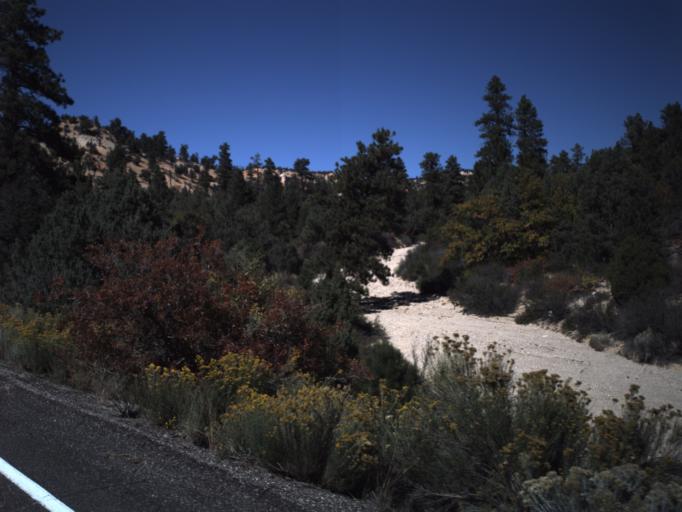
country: US
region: Utah
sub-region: Garfield County
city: Panguitch
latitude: 37.6722
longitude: -112.1121
